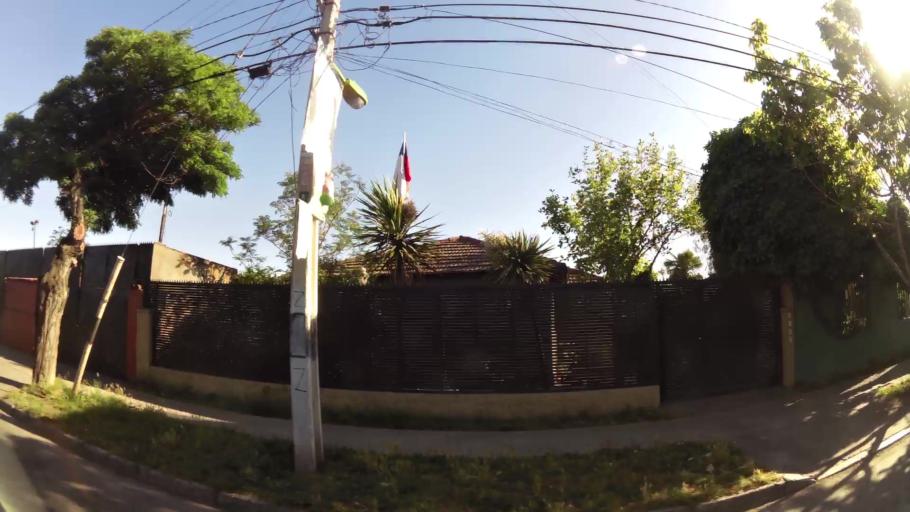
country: CL
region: Santiago Metropolitan
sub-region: Provincia de Santiago
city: La Pintana
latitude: -33.5453
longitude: -70.6717
